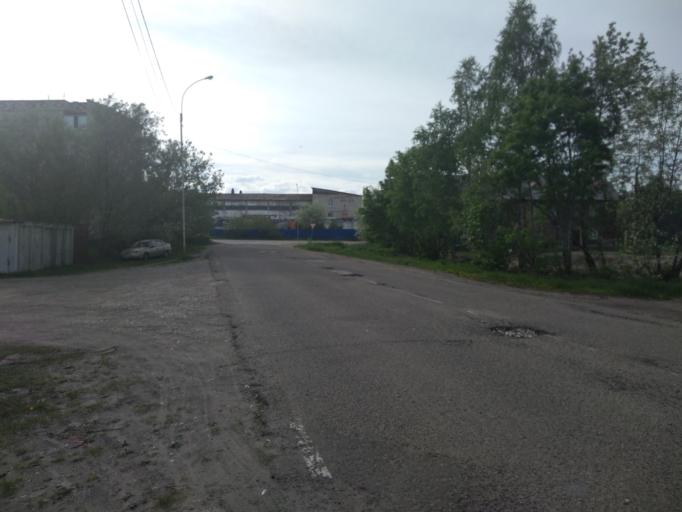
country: RU
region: Komi Republic
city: Pechora
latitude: 65.1479
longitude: 57.2154
